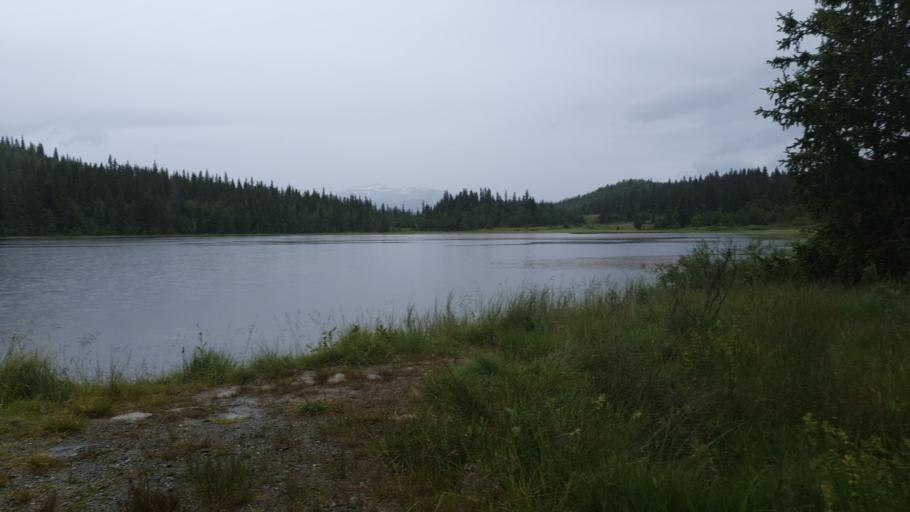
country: NO
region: Oppland
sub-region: Vestre Slidre
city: Slidre
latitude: 61.2315
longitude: 8.9238
